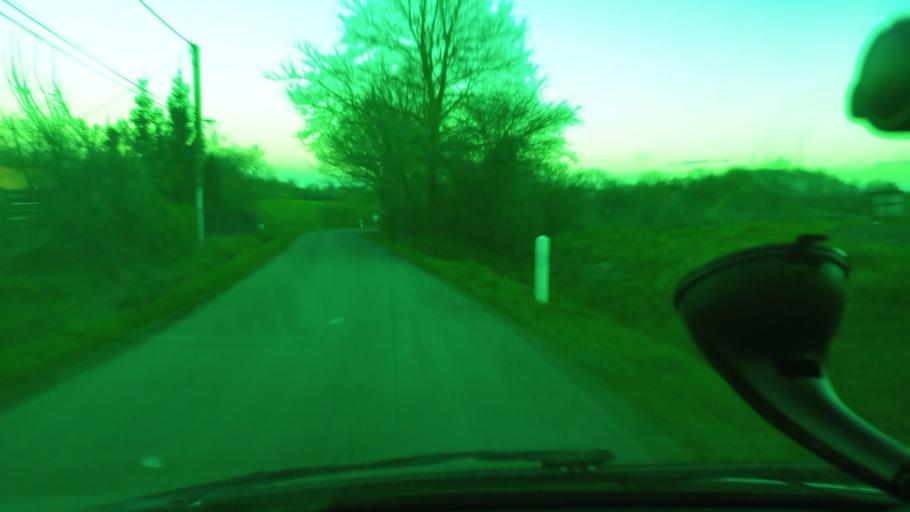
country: FR
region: Pays de la Loire
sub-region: Departement de la Vendee
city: Belleville-sur-Vie
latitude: 46.7845
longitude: -1.4037
